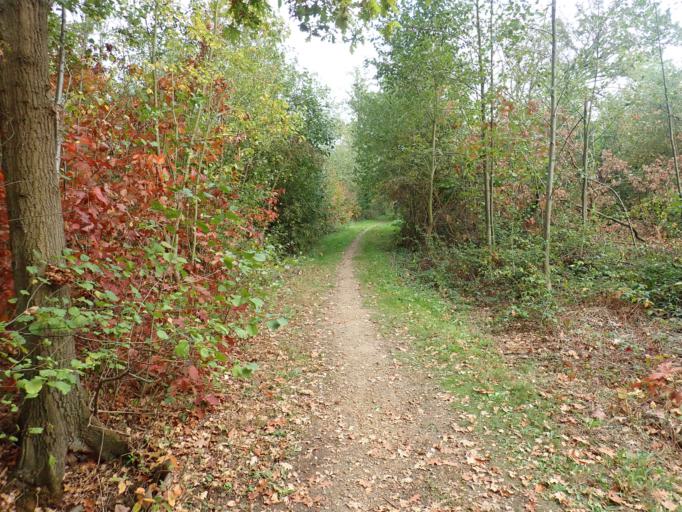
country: BE
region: Flanders
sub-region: Provincie Antwerpen
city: Herenthout
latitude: 51.1366
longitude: 4.7229
